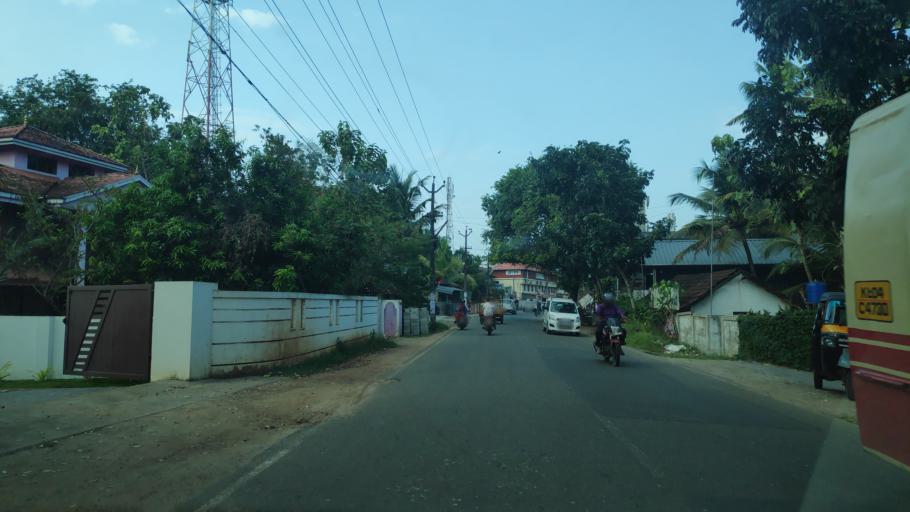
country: IN
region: Kerala
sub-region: Alappuzha
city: Alleppey
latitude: 9.5704
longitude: 76.3477
